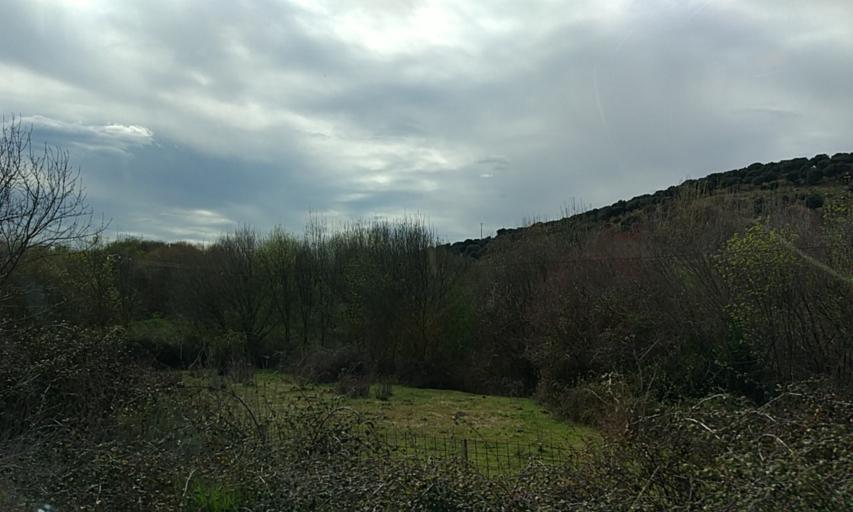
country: ES
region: Castille and Leon
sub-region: Provincia de Salamanca
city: Ciudad Rodrigo
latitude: 40.5748
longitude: -6.5412
